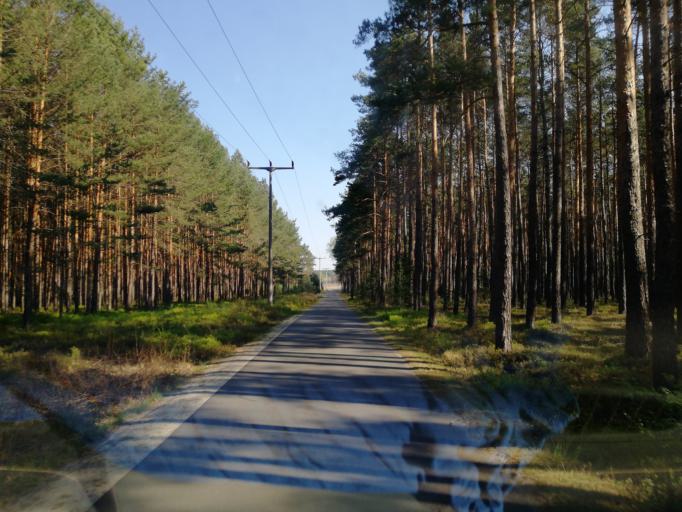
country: DE
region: Brandenburg
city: Bronkow
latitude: 51.6580
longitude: 13.8565
